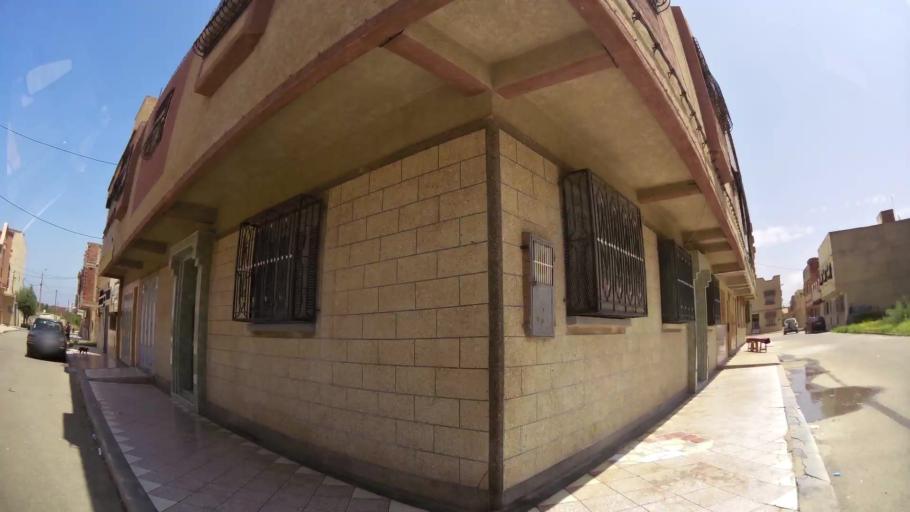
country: MA
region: Oriental
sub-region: Oujda-Angad
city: Oujda
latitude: 34.6894
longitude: -1.8906
